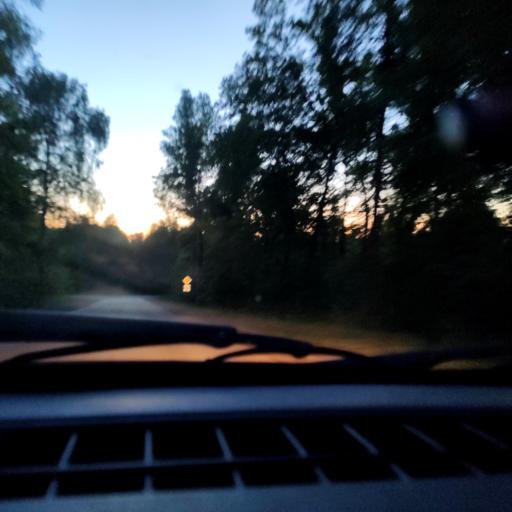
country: RU
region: Bashkortostan
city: Avdon
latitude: 54.6538
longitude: 55.5862
